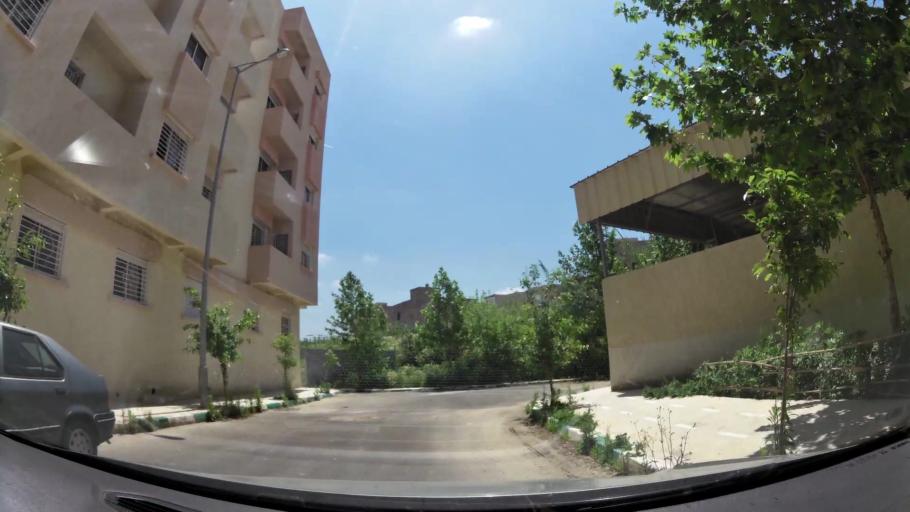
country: MA
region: Fes-Boulemane
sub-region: Fes
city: Fes
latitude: 34.0304
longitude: -5.0500
